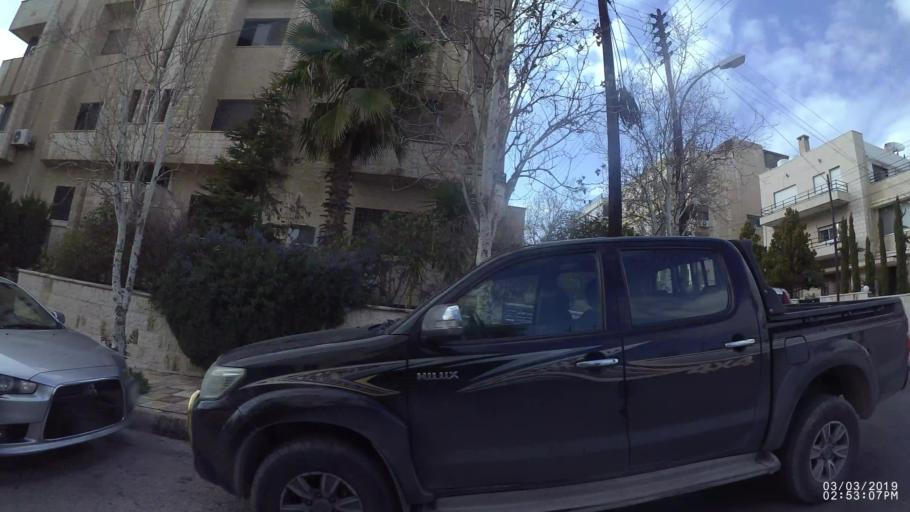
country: JO
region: Amman
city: Amman
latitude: 31.9632
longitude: 35.8949
